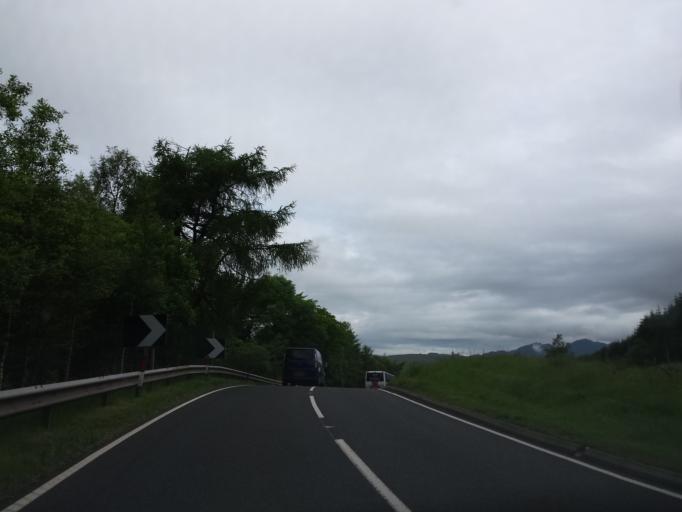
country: GB
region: Scotland
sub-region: Stirling
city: Callander
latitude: 56.4233
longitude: -4.3382
